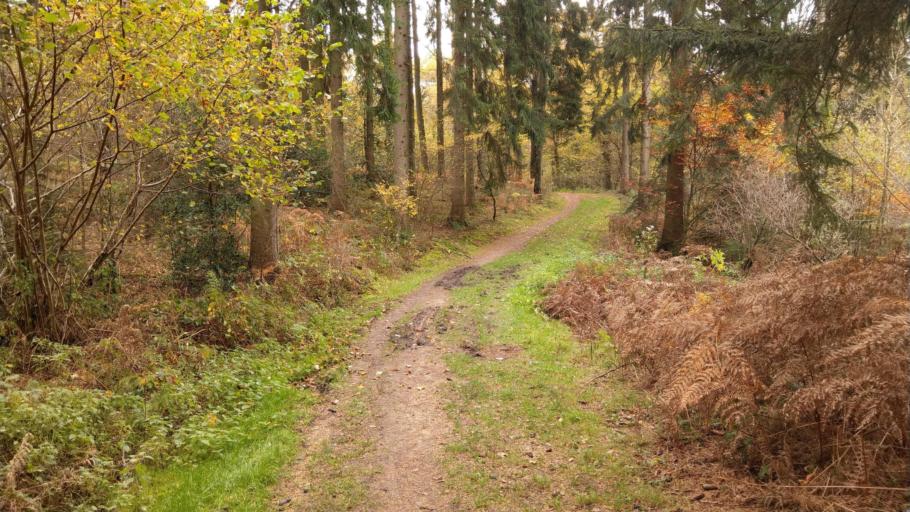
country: BE
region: Wallonia
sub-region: Province de Liege
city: La Calamine
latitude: 50.7351
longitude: 6.0107
